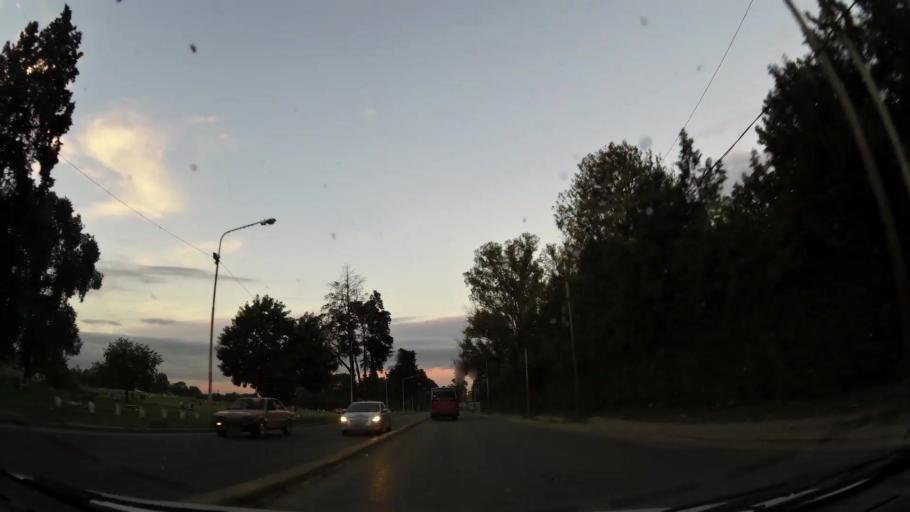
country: AR
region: Buenos Aires
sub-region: Partido de Merlo
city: Merlo
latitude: -34.6843
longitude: -58.7622
